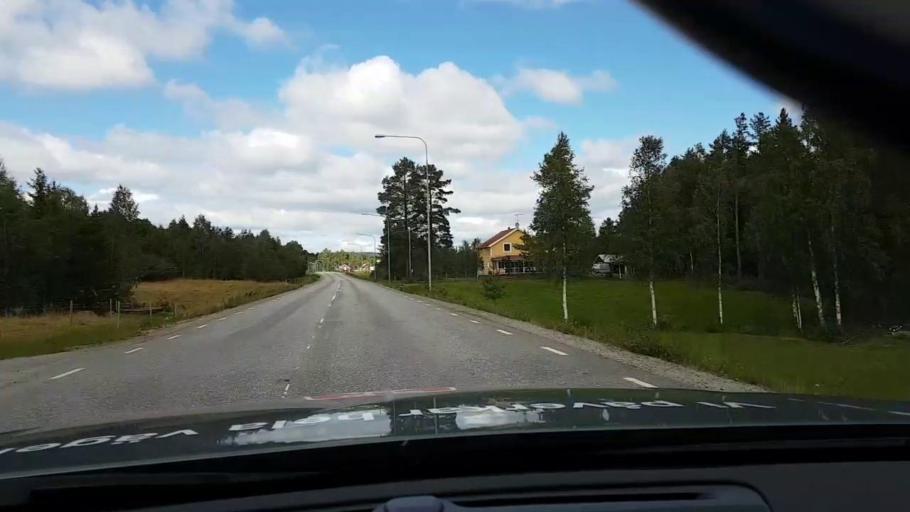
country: SE
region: Vaesternorrland
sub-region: OErnskoeldsviks Kommun
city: Bredbyn
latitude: 63.4771
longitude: 18.0942
